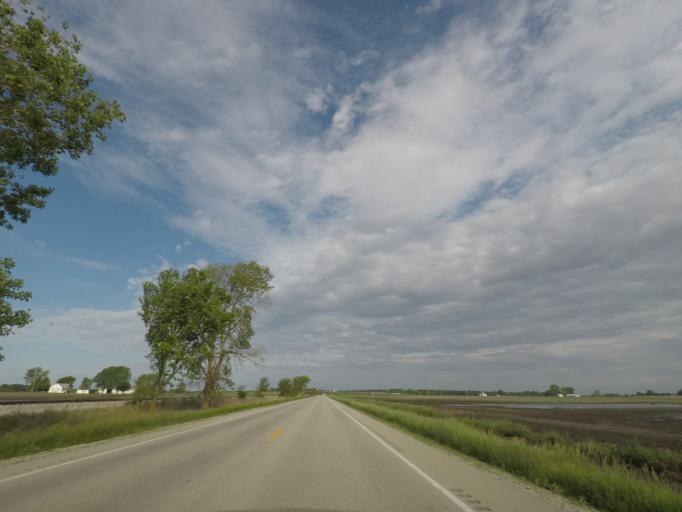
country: US
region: Illinois
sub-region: Logan County
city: Mount Pulaski
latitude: 39.9967
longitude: -89.2600
